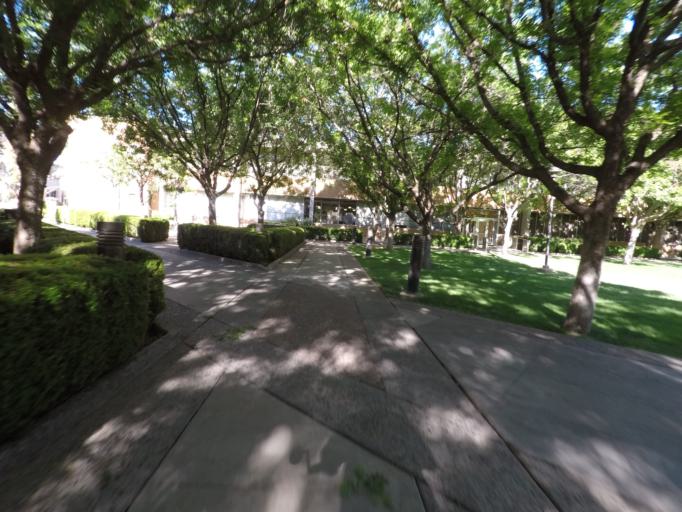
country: US
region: Arizona
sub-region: Maricopa County
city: Tempe Junction
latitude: 33.4177
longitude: -111.9360
